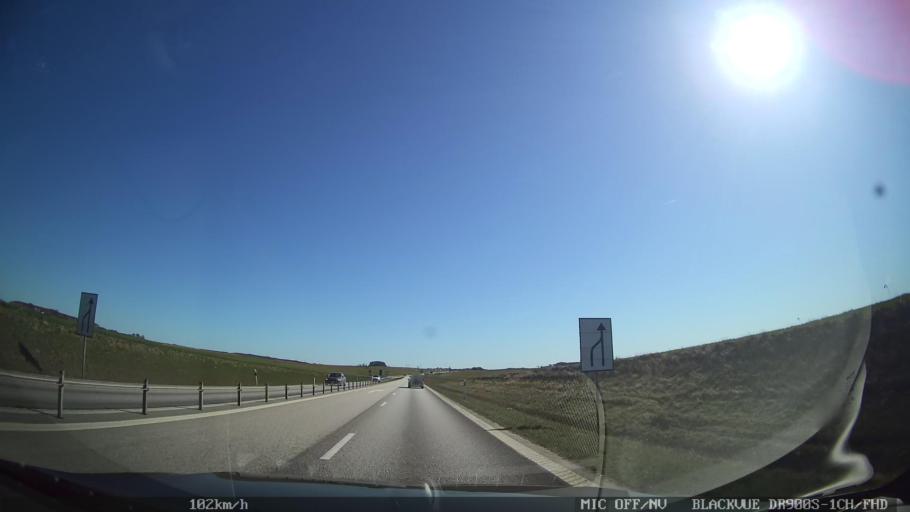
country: SE
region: Skane
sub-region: Skurups Kommun
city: Rydsgard
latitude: 55.4723
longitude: 13.6856
